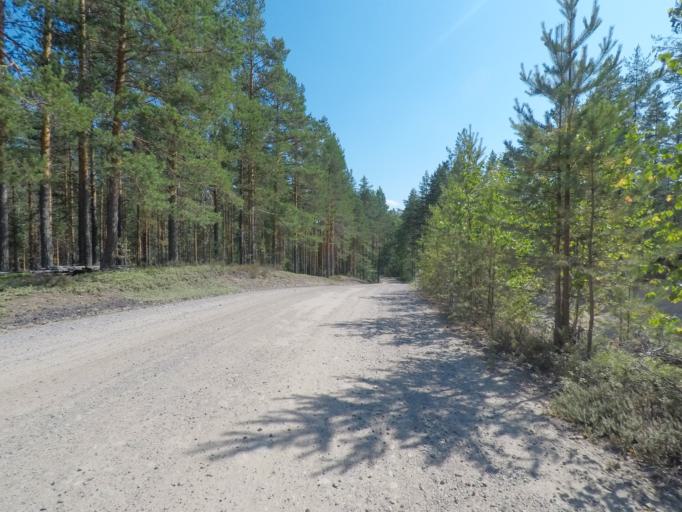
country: FI
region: Southern Savonia
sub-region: Mikkeli
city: Puumala
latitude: 61.4241
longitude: 28.0380
